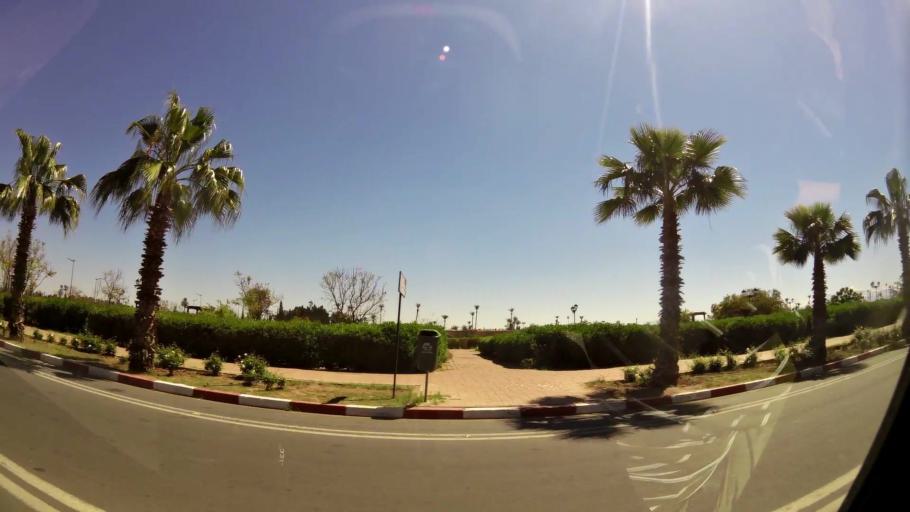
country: MA
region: Marrakech-Tensift-Al Haouz
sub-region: Marrakech
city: Marrakesh
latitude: 31.5999
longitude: -7.9874
